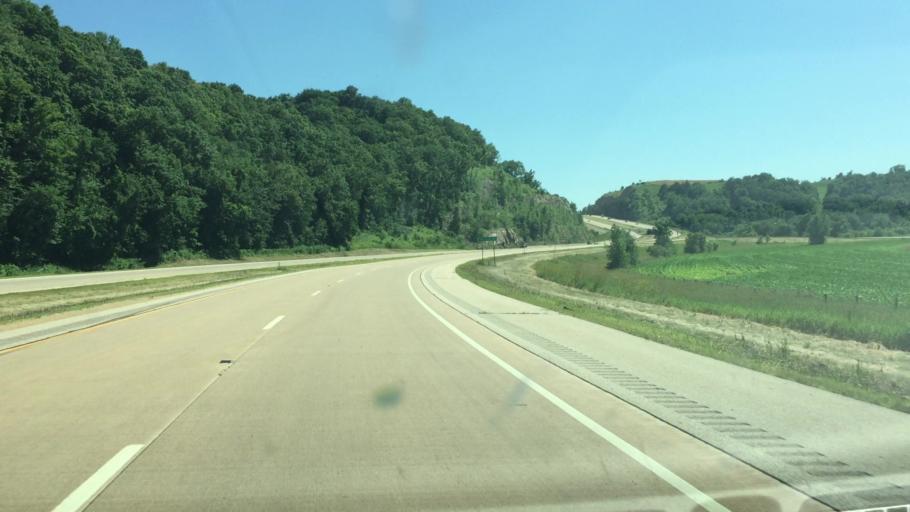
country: US
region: Wisconsin
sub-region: Grant County
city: Dickeyville
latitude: 42.6497
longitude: -90.5741
